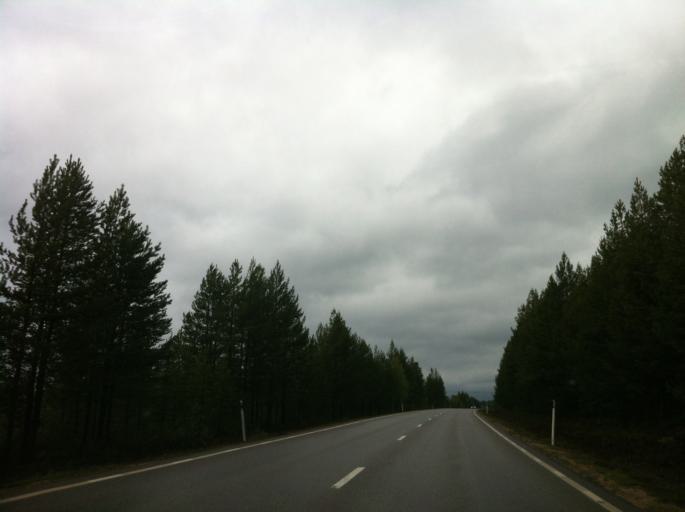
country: SE
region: Jaemtland
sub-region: Harjedalens Kommun
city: Sveg
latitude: 62.0510
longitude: 14.3129
